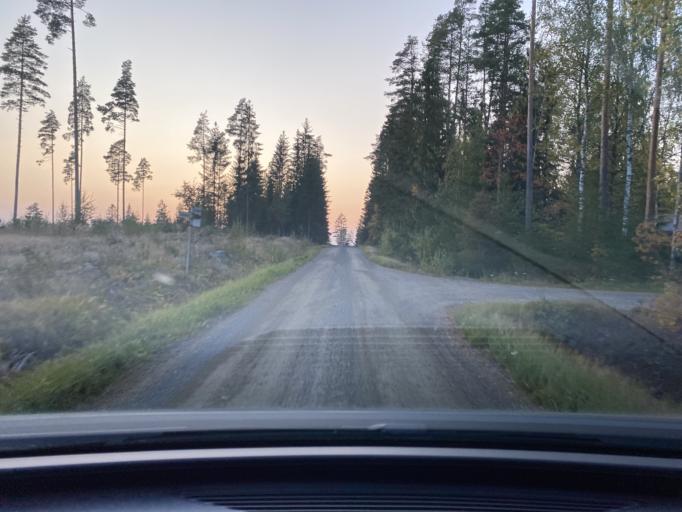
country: FI
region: Pirkanmaa
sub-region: Lounais-Pirkanmaa
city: Punkalaidun
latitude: 61.1097
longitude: 23.2310
